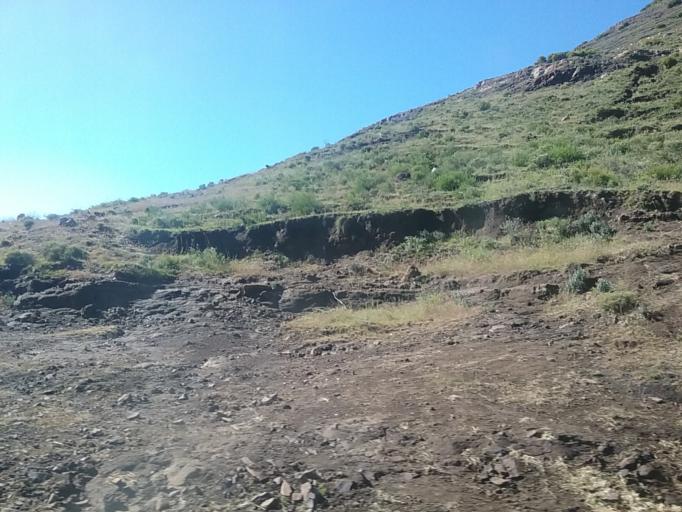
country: LS
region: Berea
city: Teyateyaneng
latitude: -29.2360
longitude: 27.9134
